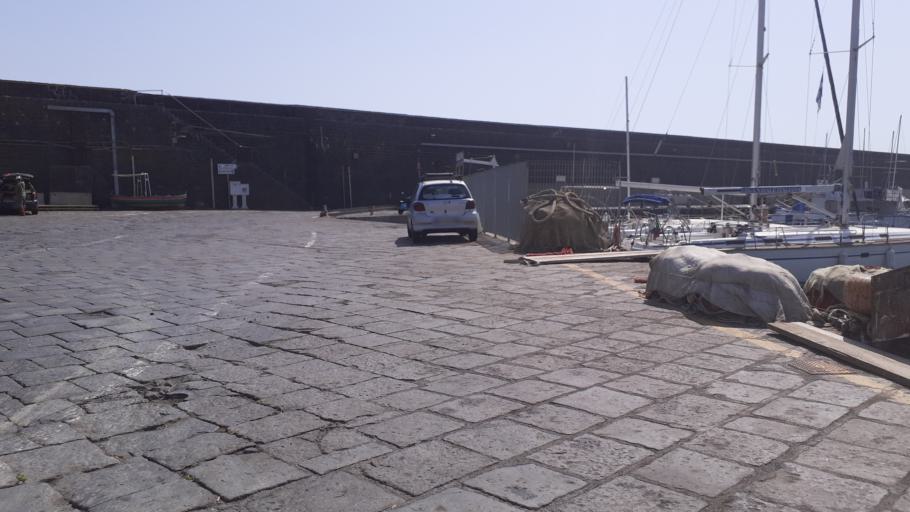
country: IT
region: Sicily
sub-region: Catania
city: Catania
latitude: 37.5015
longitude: 15.0970
